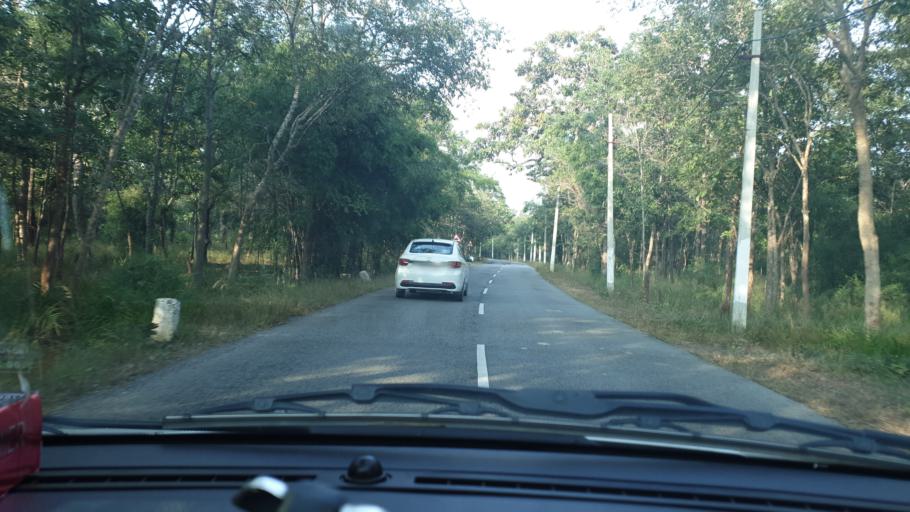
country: IN
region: Andhra Pradesh
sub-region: Kurnool
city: Srisailam
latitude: 16.3037
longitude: 78.7318
